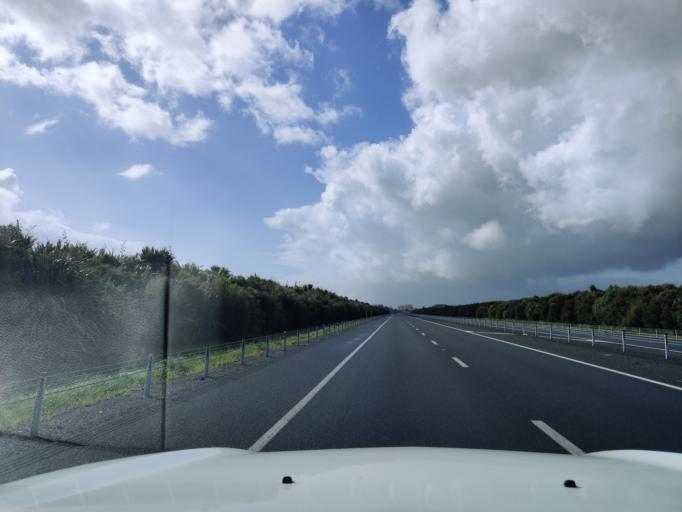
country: NZ
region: Waikato
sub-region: Waipa District
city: Cambridge
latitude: -37.8744
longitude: 175.4817
